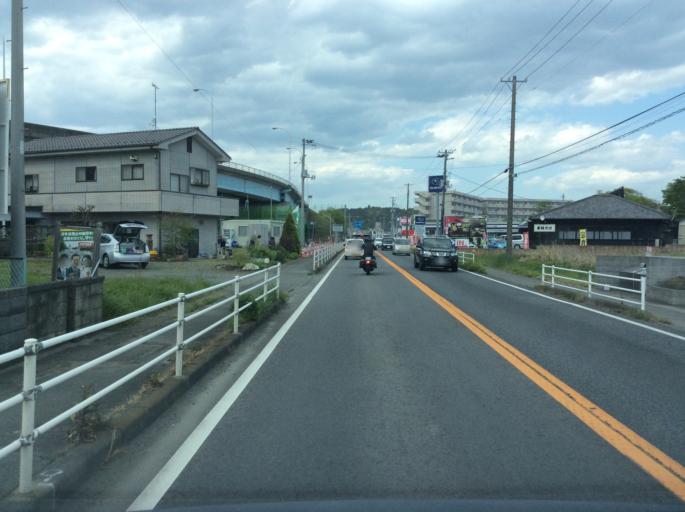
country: JP
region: Ibaraki
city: Kitaibaraki
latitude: 36.8782
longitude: 140.7883
